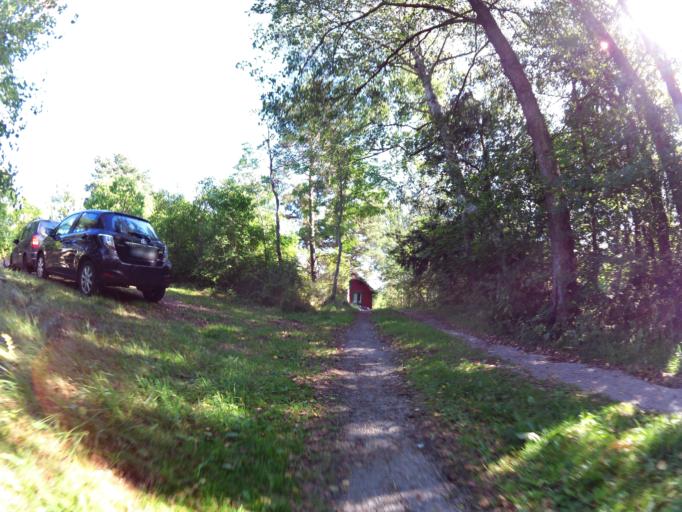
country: NO
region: Ostfold
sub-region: Fredrikstad
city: Fredrikstad
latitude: 59.1720
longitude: 10.8455
